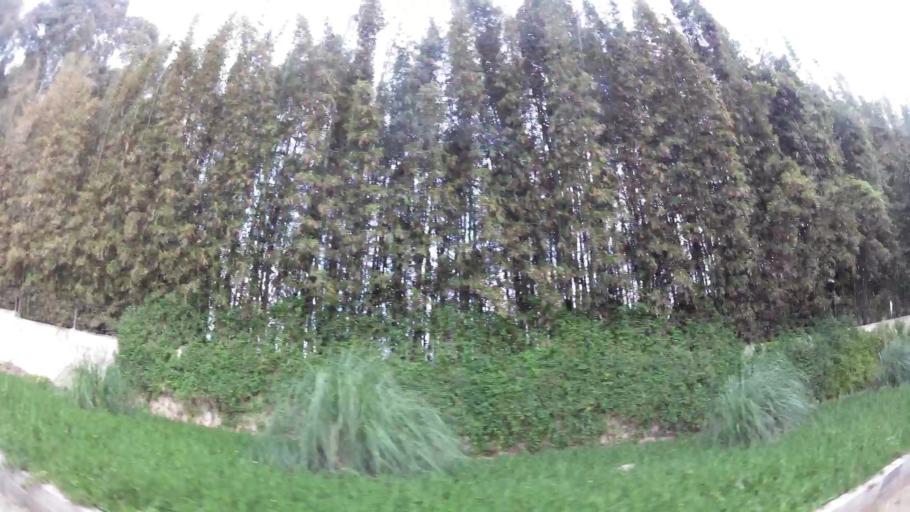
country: MA
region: Rabat-Sale-Zemmour-Zaer
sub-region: Skhirate-Temara
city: Temara
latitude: 33.9476
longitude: -6.8439
